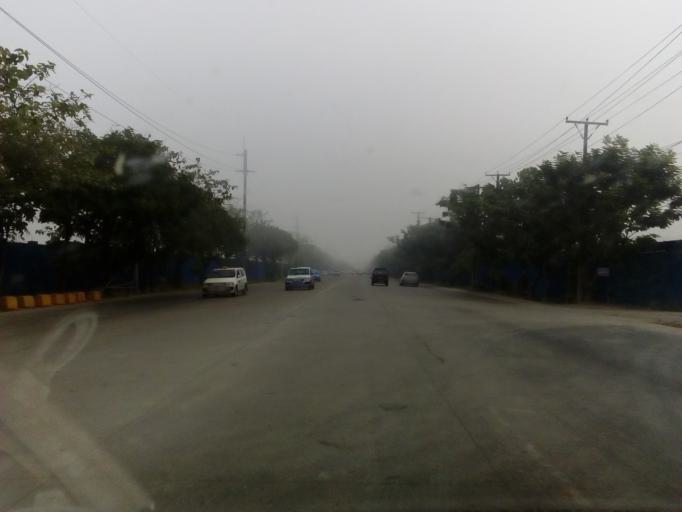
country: MM
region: Yangon
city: Yangon
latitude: 16.8135
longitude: 96.1875
